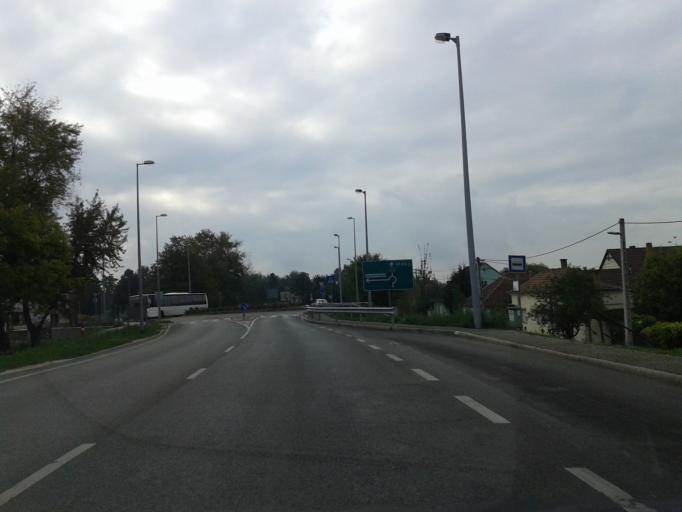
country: HU
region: Csongrad
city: Szeged
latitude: 46.2361
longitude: 20.1710
